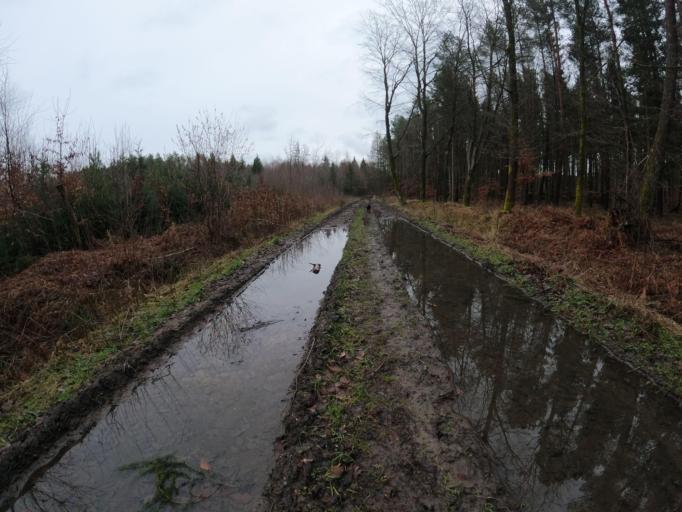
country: PL
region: West Pomeranian Voivodeship
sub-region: Powiat slawienski
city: Darlowo
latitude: 54.3932
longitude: 16.4953
